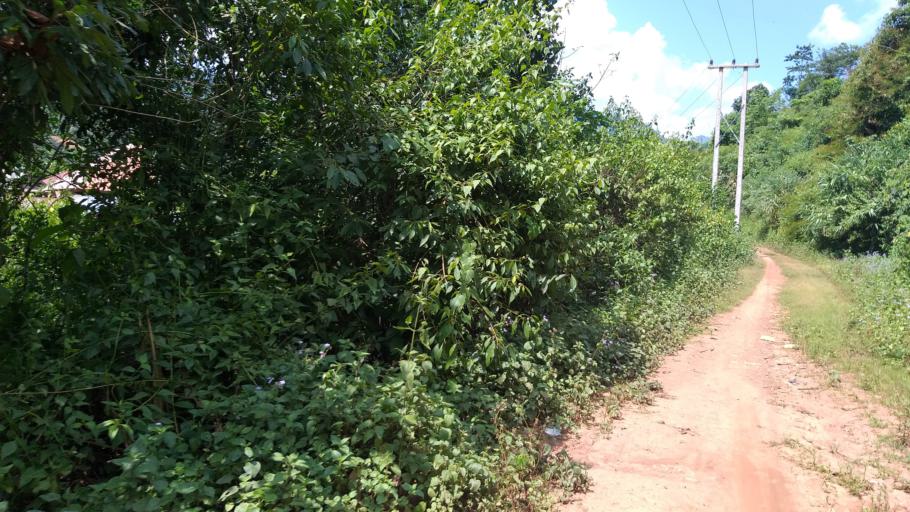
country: LA
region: Phongsali
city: Khoa
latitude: 21.3681
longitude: 102.5339
